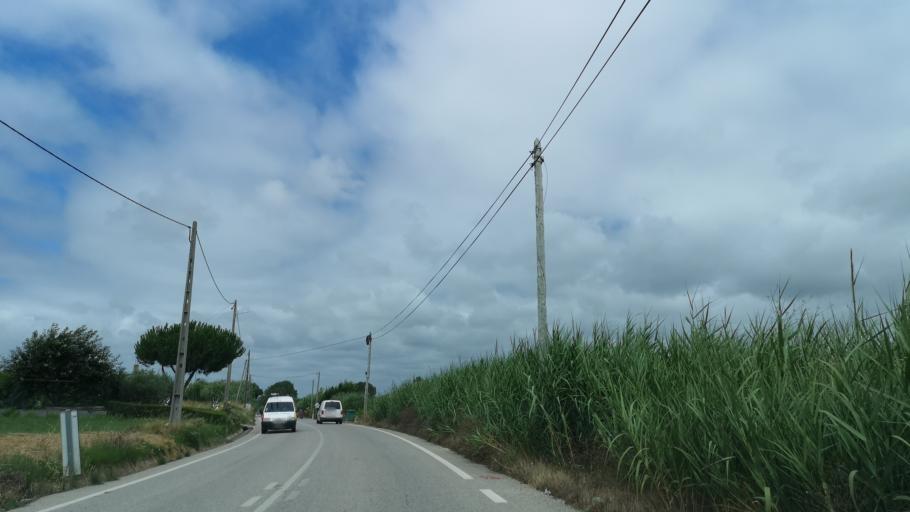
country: PT
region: Leiria
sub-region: Nazare
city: Nazare
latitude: 39.5468
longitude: -9.0767
